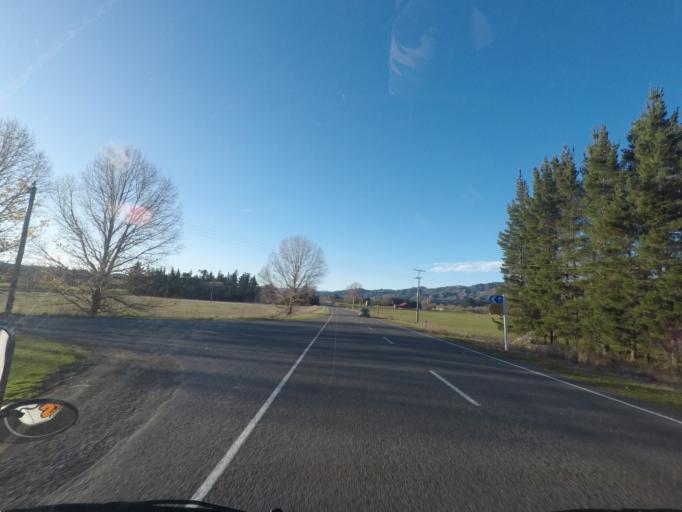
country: NZ
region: Canterbury
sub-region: Kaikoura District
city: Kaikoura
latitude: -42.7185
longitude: 173.2868
